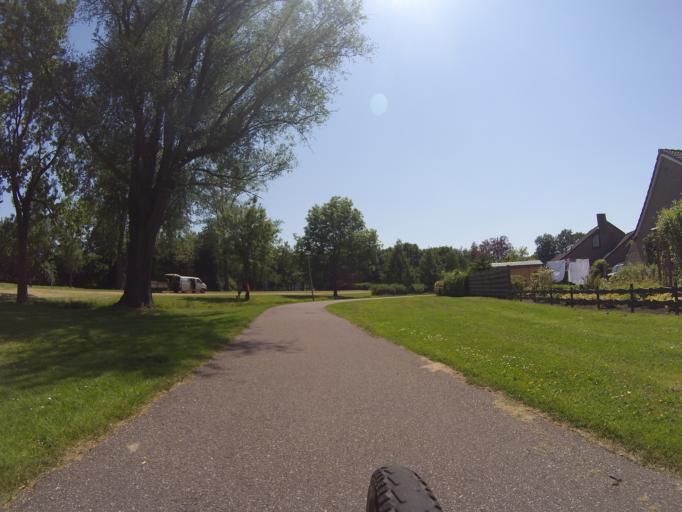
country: NL
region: Drenthe
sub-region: Gemeente Emmen
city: Schoonebeek
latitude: 52.6656
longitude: 6.8860
